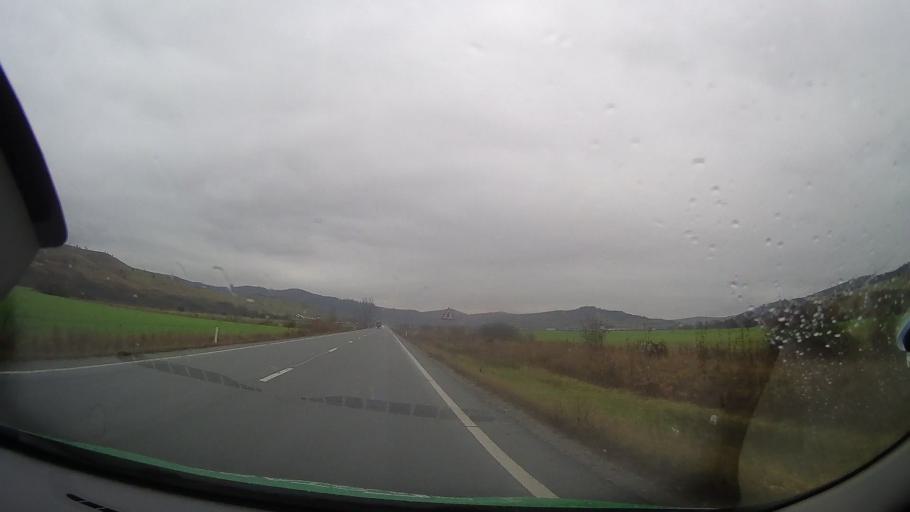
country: RO
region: Bistrita-Nasaud
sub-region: Comuna Teaca
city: Teaca
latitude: 46.9260
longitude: 24.4862
